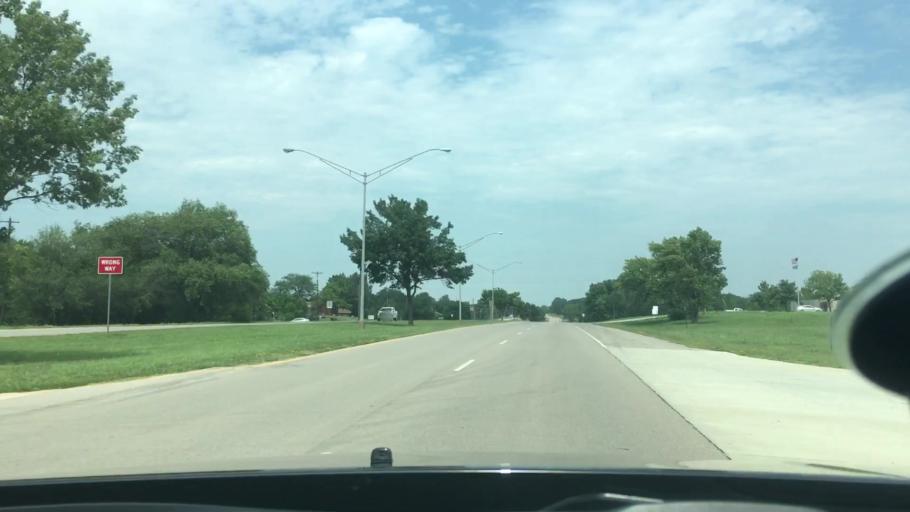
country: US
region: Oklahoma
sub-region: Pontotoc County
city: Ada
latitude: 34.8040
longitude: -96.6782
